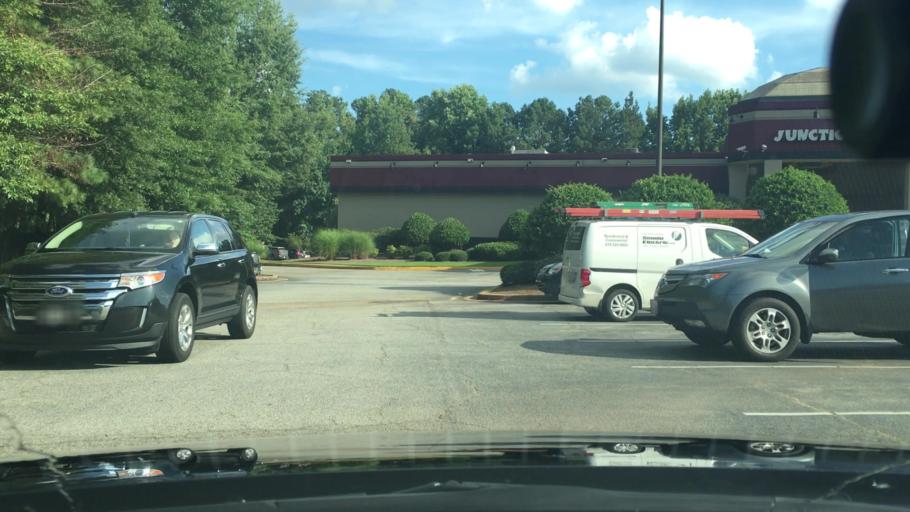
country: US
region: Georgia
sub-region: Coweta County
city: East Newnan
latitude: 33.3971
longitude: -84.7336
